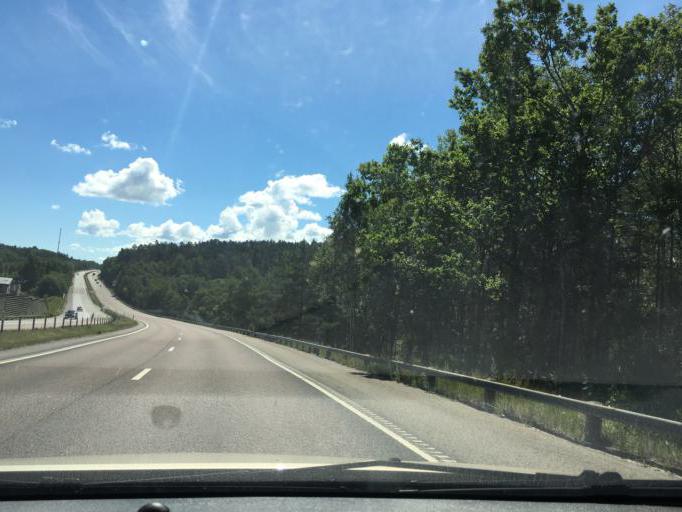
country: SE
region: Stockholm
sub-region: Nacka Kommun
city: Nacka
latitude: 59.3028
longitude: 18.1844
